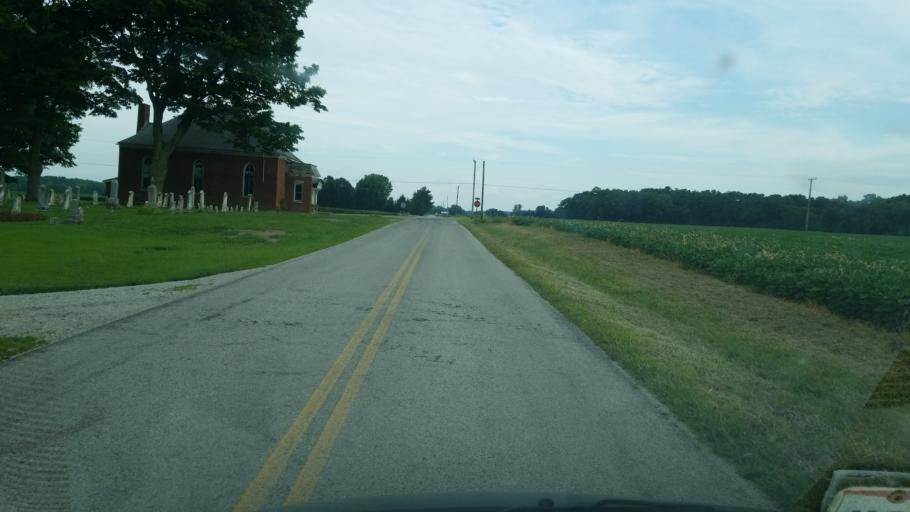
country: US
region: Ohio
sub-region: Seneca County
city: Tiffin
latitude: 41.0220
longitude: -83.0546
